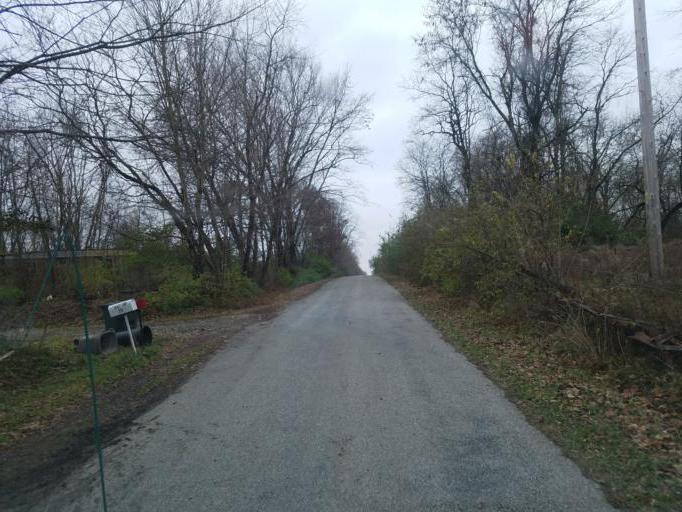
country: US
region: Ohio
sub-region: Morrow County
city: Cardington
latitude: 40.4126
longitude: -82.8517
